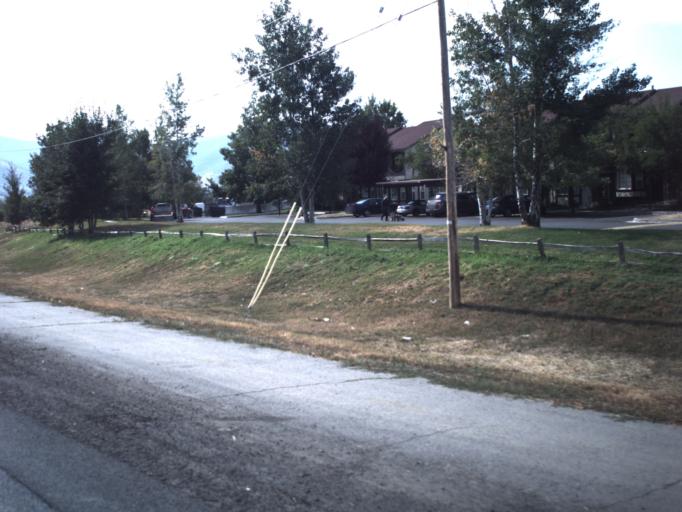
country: US
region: Utah
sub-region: Wasatch County
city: Midway
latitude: 40.5108
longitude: -111.4537
